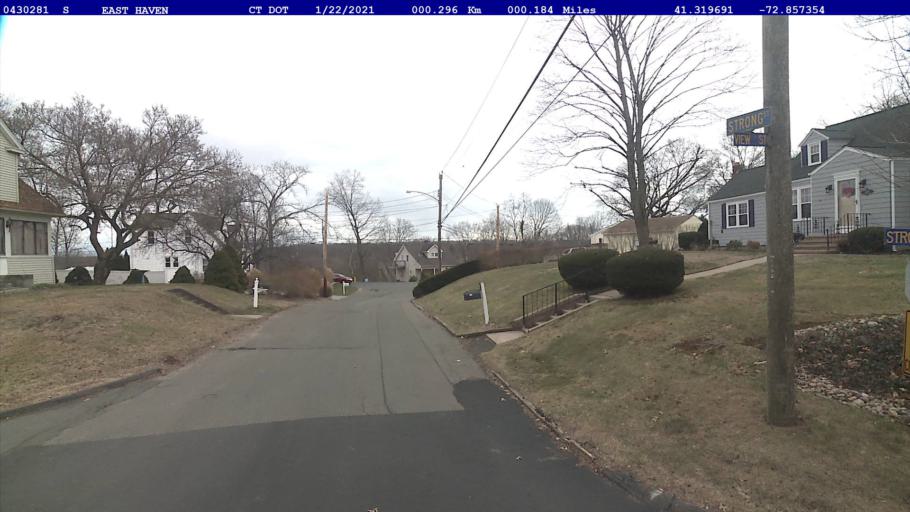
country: US
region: Connecticut
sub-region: New Haven County
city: East Haven
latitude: 41.3197
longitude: -72.8574
